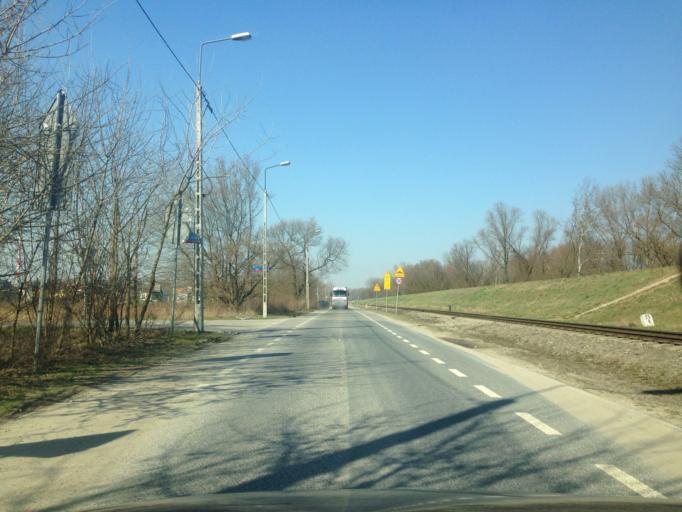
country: PL
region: Masovian Voivodeship
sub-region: Warszawa
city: Wilanow
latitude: 52.1762
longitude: 21.1171
